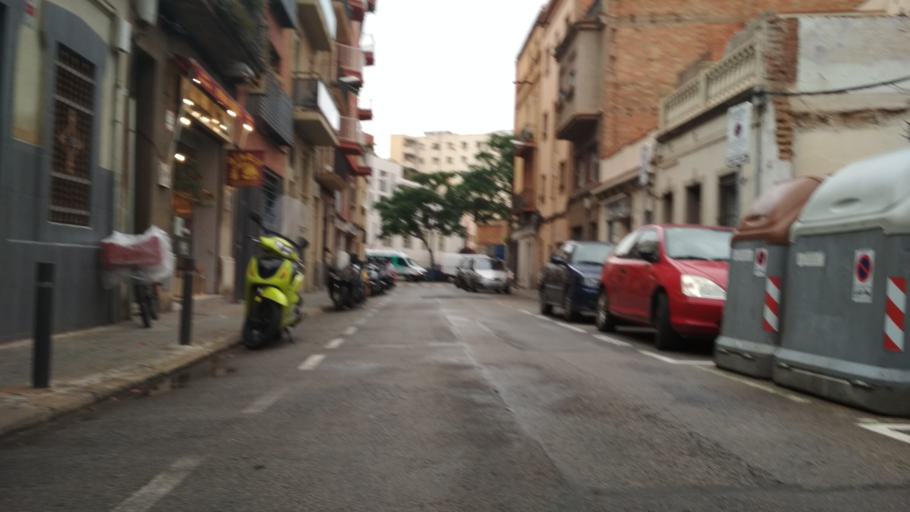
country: ES
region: Catalonia
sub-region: Provincia de Barcelona
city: Sant Marti
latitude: 41.4160
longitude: 2.1847
